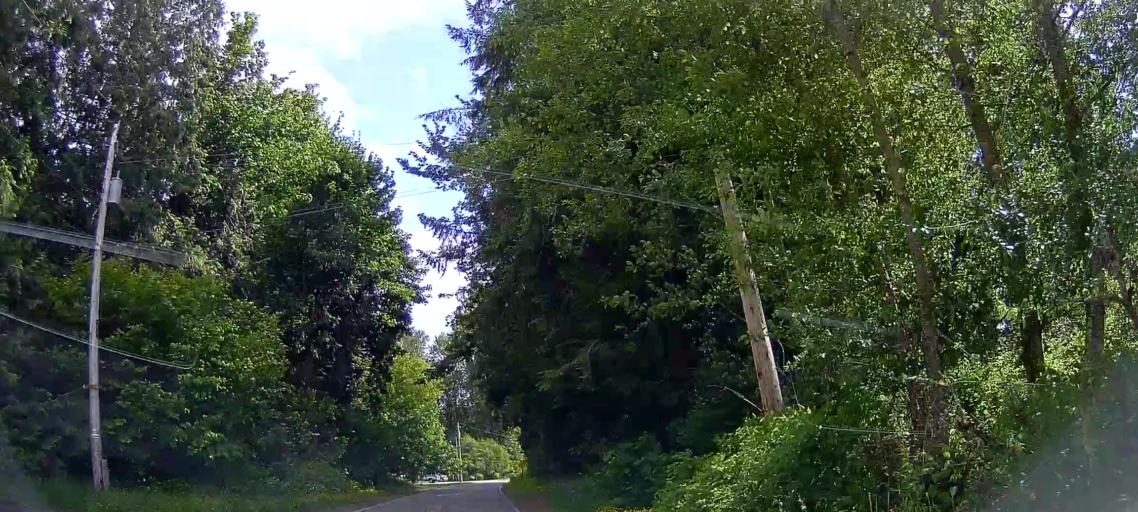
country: US
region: Washington
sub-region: Skagit County
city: Sedro-Woolley
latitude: 48.5599
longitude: -122.2109
